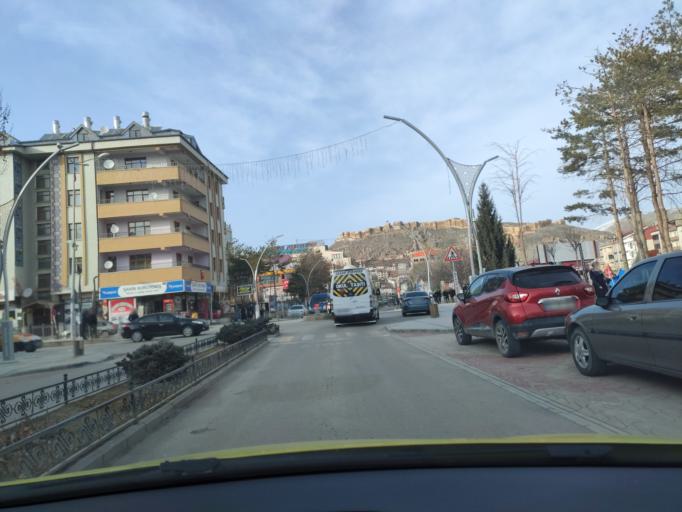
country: TR
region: Bayburt
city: Bayburt
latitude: 40.2565
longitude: 40.2258
